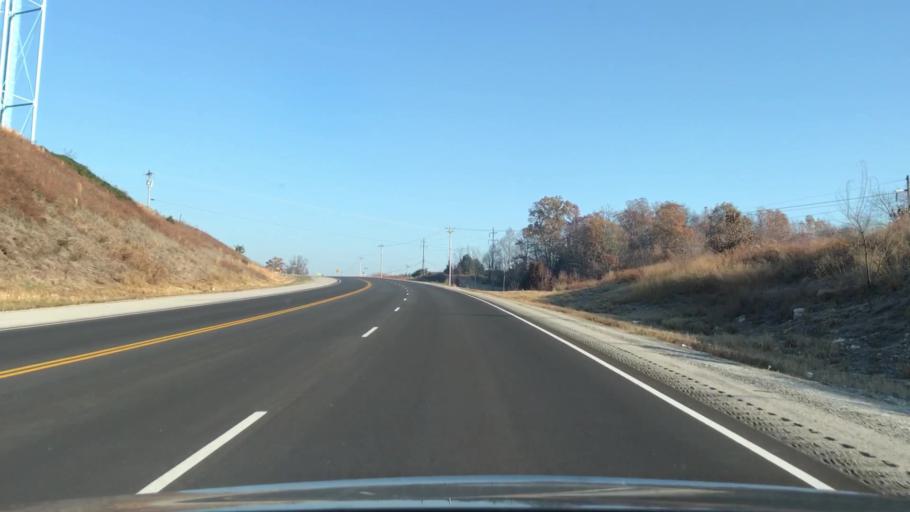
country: US
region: Kentucky
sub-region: Edmonson County
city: Brownsville
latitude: 37.1000
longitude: -86.2302
